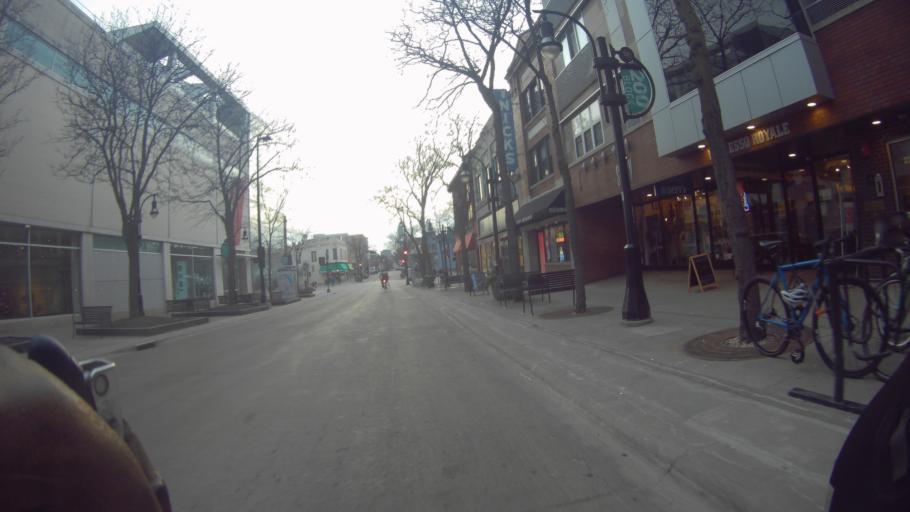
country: US
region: Wisconsin
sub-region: Dane County
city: Madison
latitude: 43.0748
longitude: -89.3890
